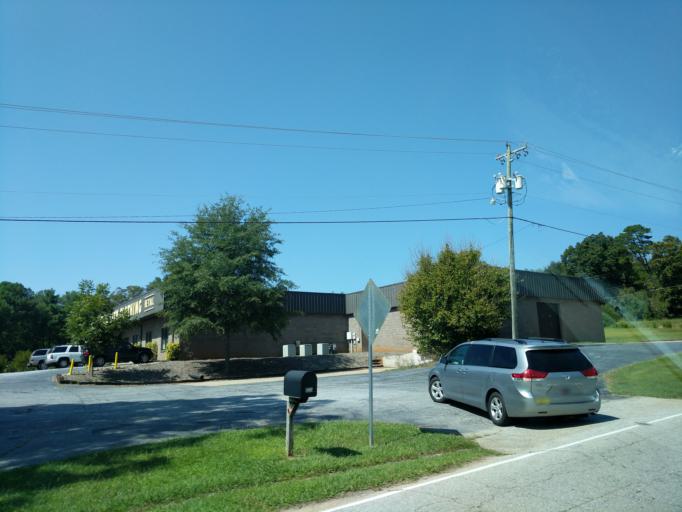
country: US
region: South Carolina
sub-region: Spartanburg County
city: Valley Falls
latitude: 35.0036
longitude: -81.9262
